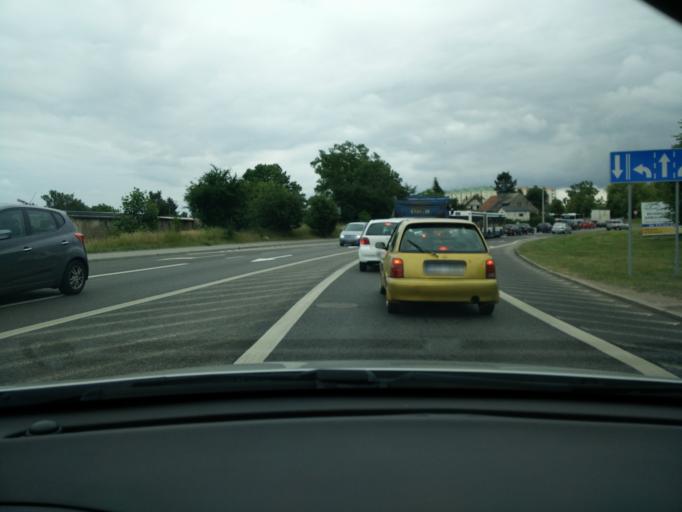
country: PL
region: Pomeranian Voivodeship
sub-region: Gdynia
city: Pogorze
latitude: 54.5623
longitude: 18.5093
